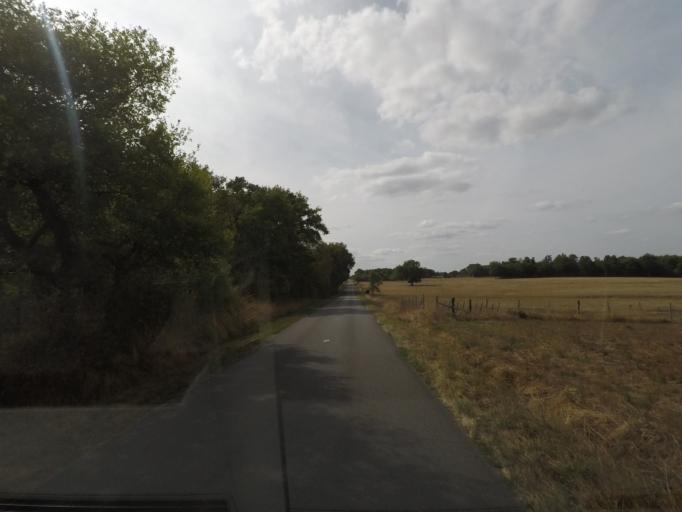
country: FR
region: Poitou-Charentes
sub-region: Departement de la Charente
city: Loubert
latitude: 45.9417
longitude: 0.5217
